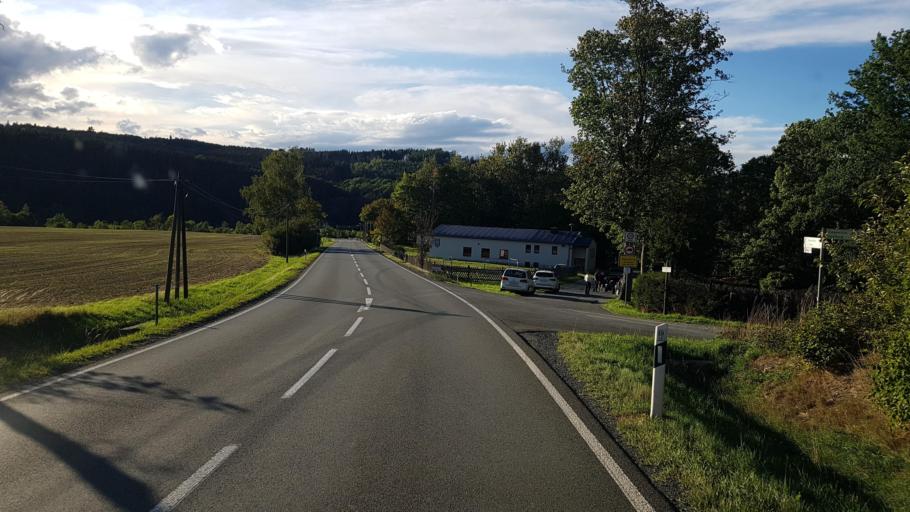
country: DE
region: Thuringia
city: Harra
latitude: 50.4512
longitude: 11.6992
